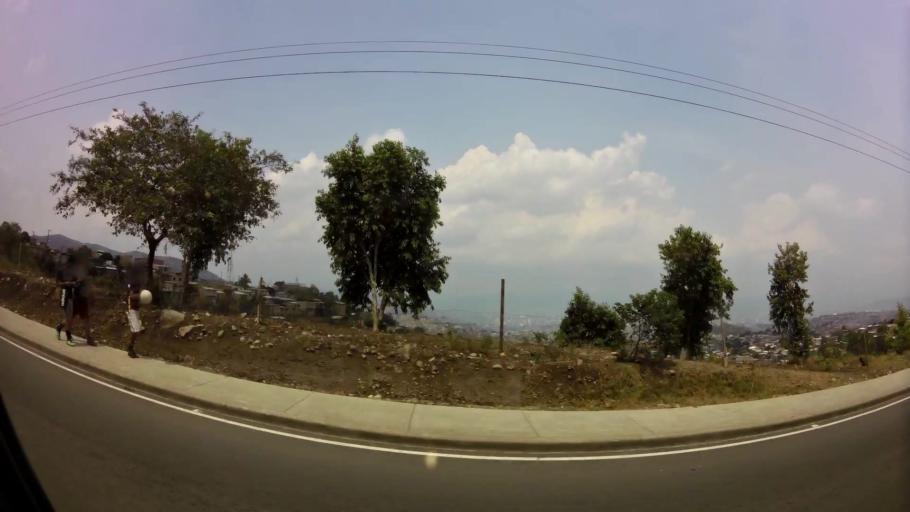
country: HN
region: Francisco Morazan
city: El Lolo
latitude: 14.0988
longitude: -87.2520
